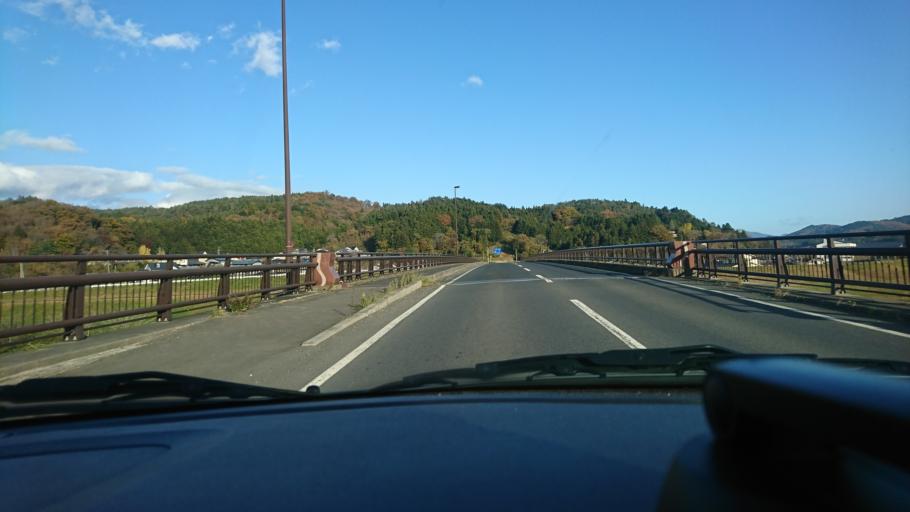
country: JP
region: Iwate
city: Ichinoseki
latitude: 38.9033
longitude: 141.2576
